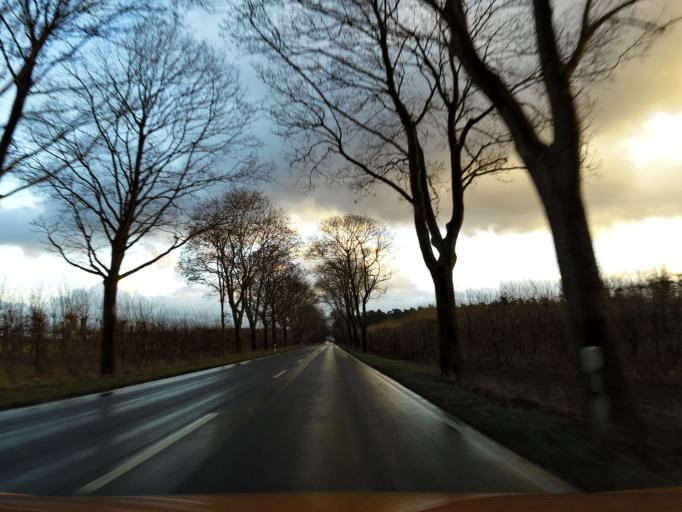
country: DE
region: Lower Saxony
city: Hillerse
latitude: 52.4012
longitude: 10.3651
